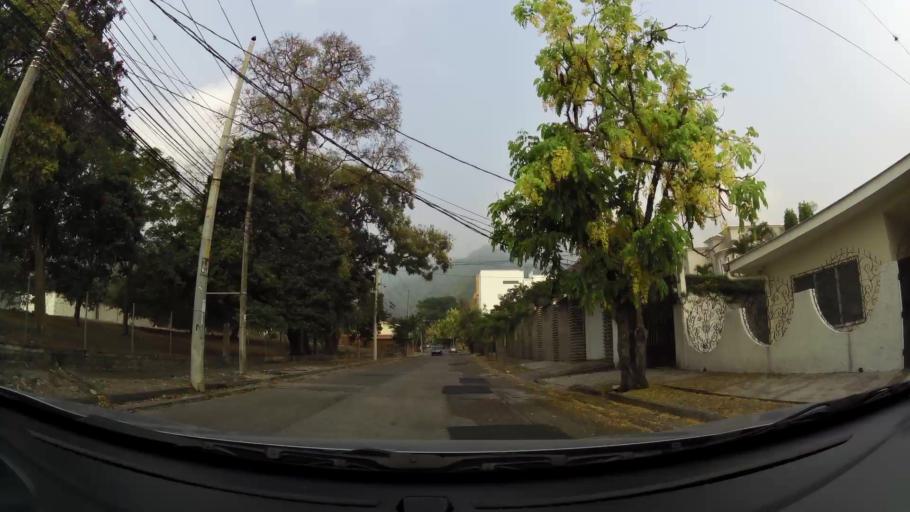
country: HN
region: Cortes
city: Armenta
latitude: 15.5029
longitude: -88.0460
